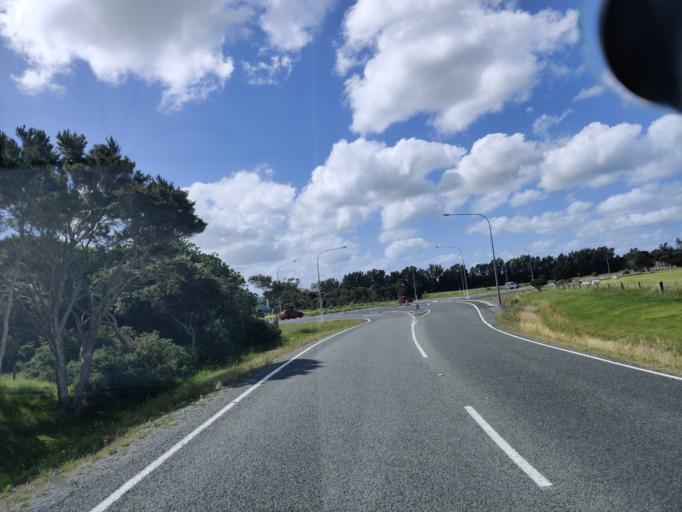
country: NZ
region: Northland
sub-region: Whangarei
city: Ruakaka
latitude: -35.9649
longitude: 174.4462
